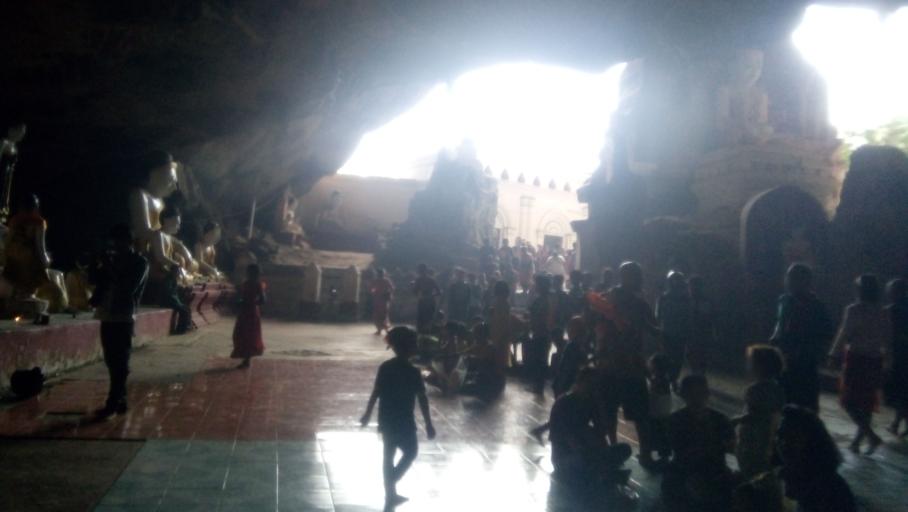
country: MM
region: Kayin
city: Hpa-an
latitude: 16.8230
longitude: 97.5855
